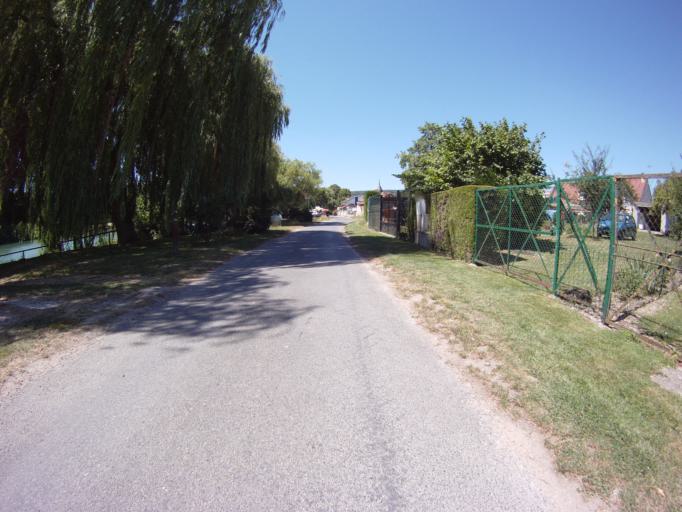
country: FR
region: Champagne-Ardenne
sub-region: Departement de la Marne
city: Damery
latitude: 49.0683
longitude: 3.8805
